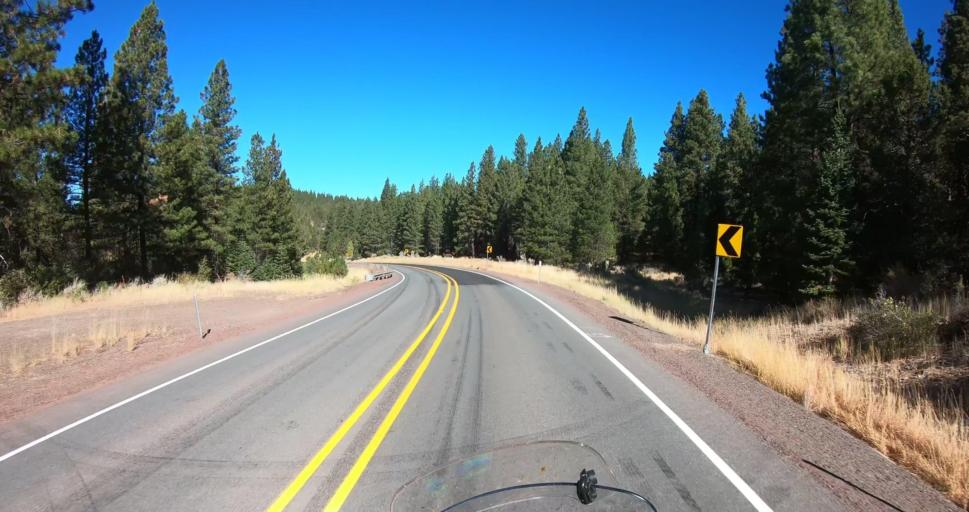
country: US
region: Oregon
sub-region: Lake County
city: Lakeview
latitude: 42.2489
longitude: -120.3145
